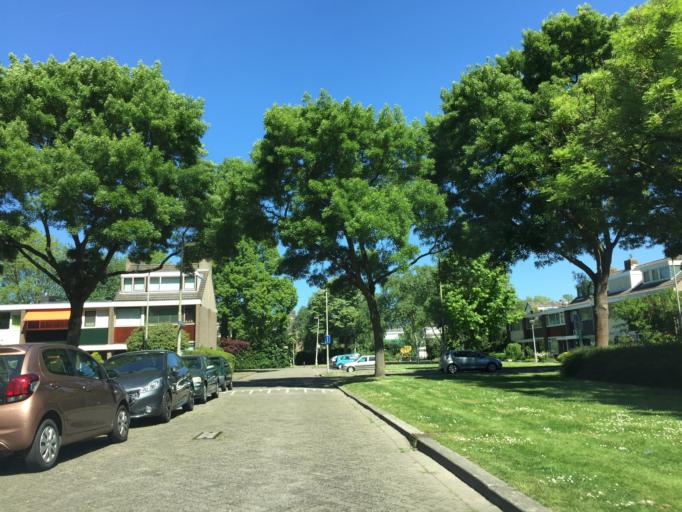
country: NL
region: South Holland
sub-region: Gemeente Rotterdam
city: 's-Gravenland
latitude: 51.9389
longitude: 4.5406
